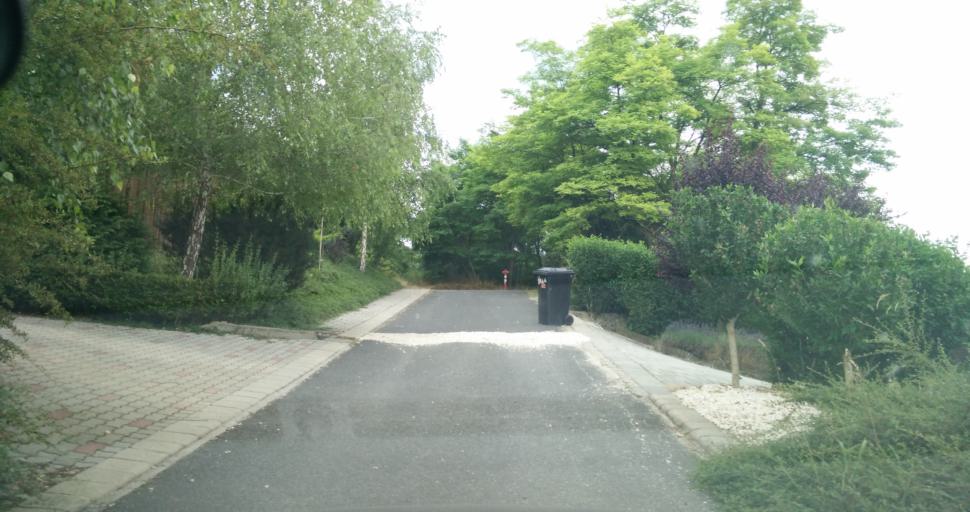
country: HU
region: Pest
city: Piliscsaba
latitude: 47.6418
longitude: 18.7924
